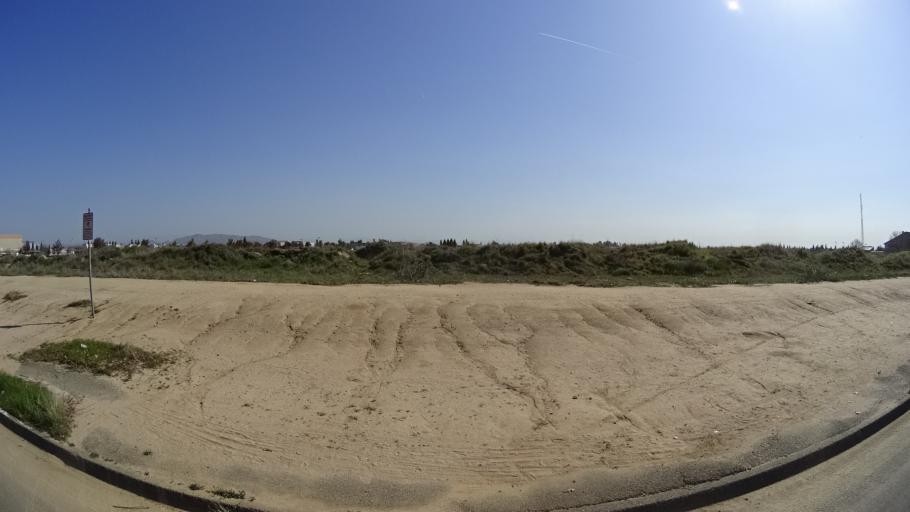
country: US
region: California
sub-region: Fresno County
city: Clovis
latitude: 36.8861
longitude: -119.7387
